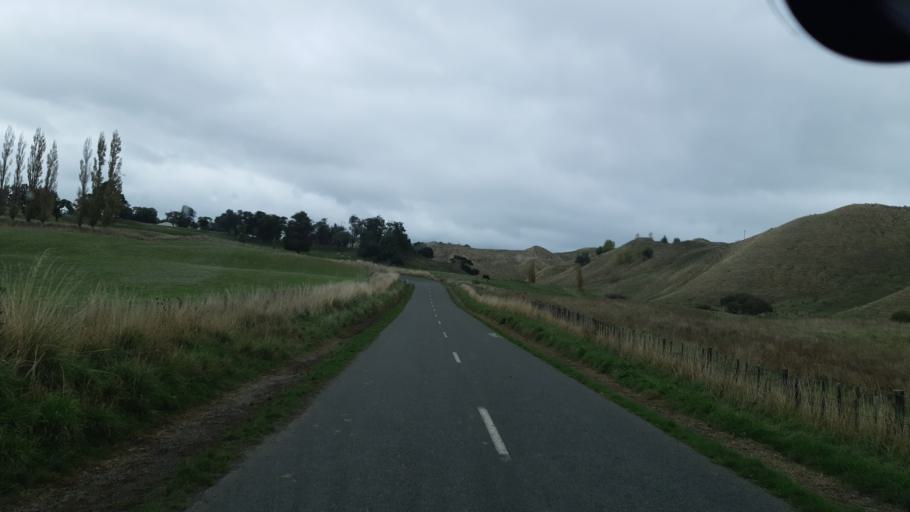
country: NZ
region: Manawatu-Wanganui
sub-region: Ruapehu District
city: Waiouru
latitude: -39.6189
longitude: 175.6178
